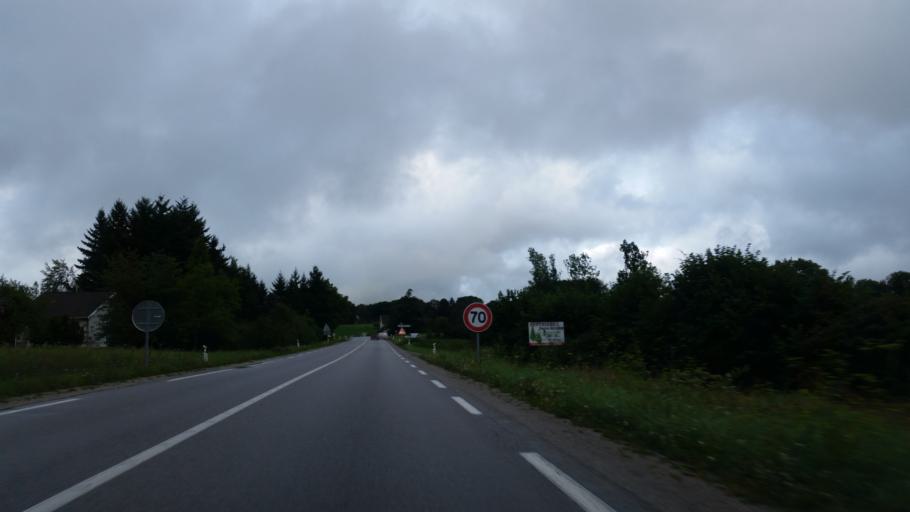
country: FR
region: Franche-Comte
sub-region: Departement de la Haute-Saone
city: Fougerolles
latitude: 47.9229
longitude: 6.4210
